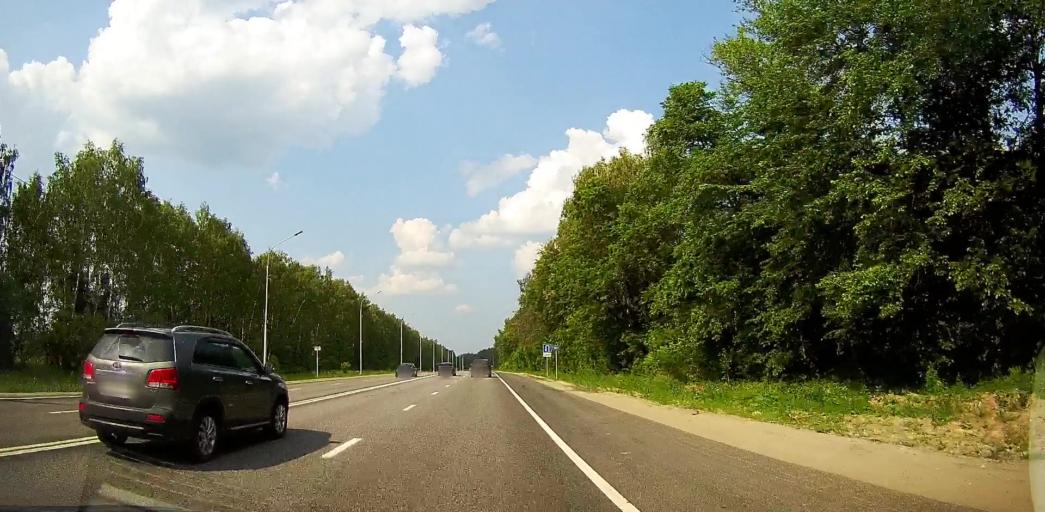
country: RU
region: Moskovskaya
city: Mikhnevo
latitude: 55.0828
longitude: 37.9539
